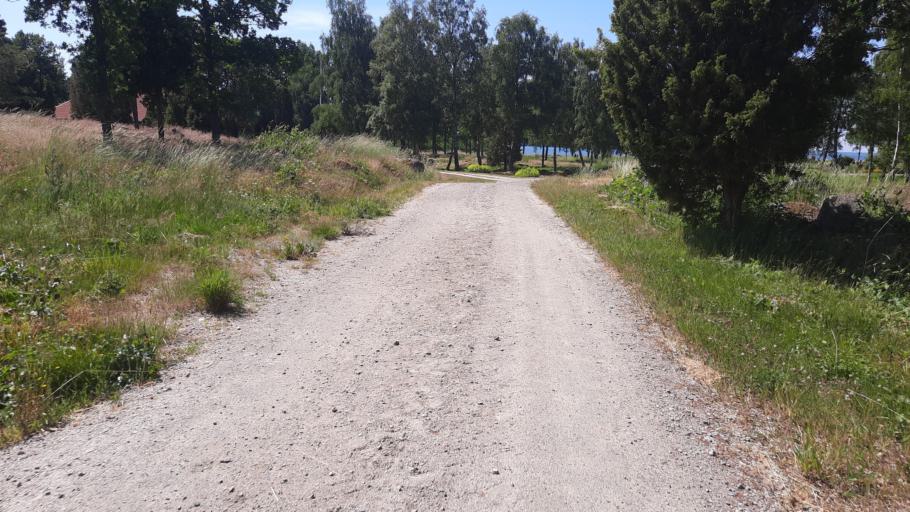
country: SE
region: Blekinge
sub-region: Karlskrona Kommun
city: Jaemjoe
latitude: 56.1482
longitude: 15.7502
